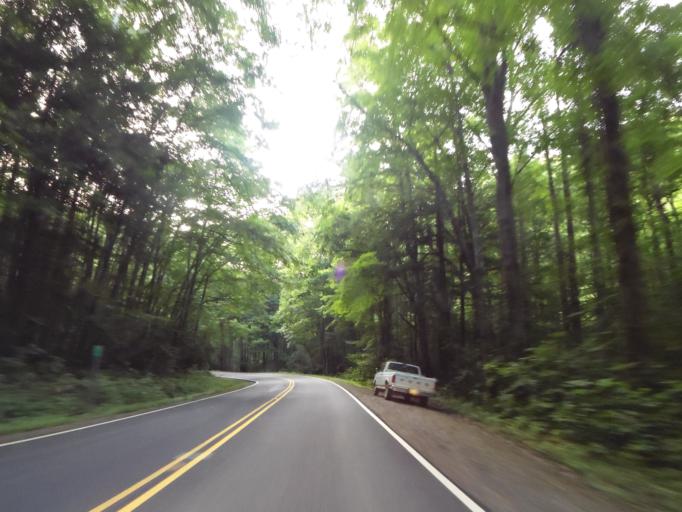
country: US
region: Tennessee
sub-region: Johnson County
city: Mountain City
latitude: 36.5757
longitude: -81.8484
